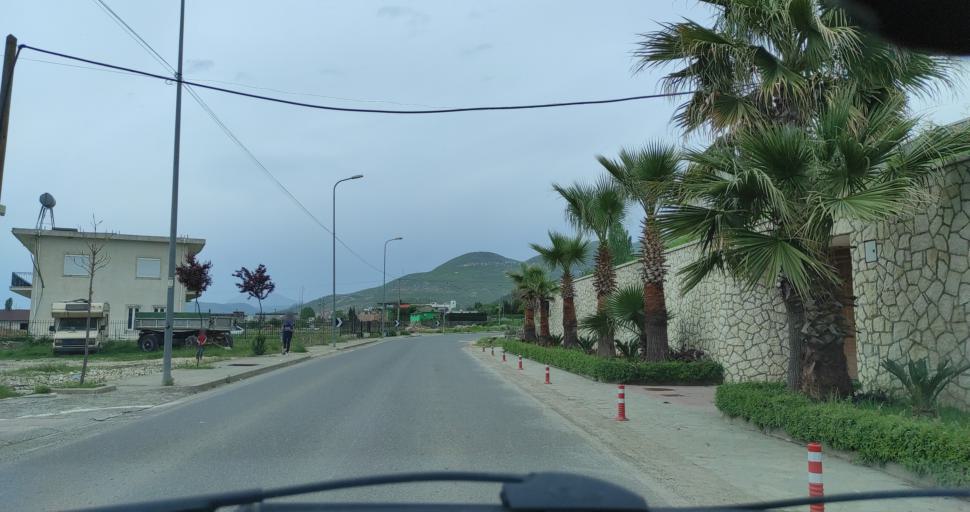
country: AL
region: Lezhe
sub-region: Rrethi i Kurbinit
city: Lac
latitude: 41.6249
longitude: 19.7089
